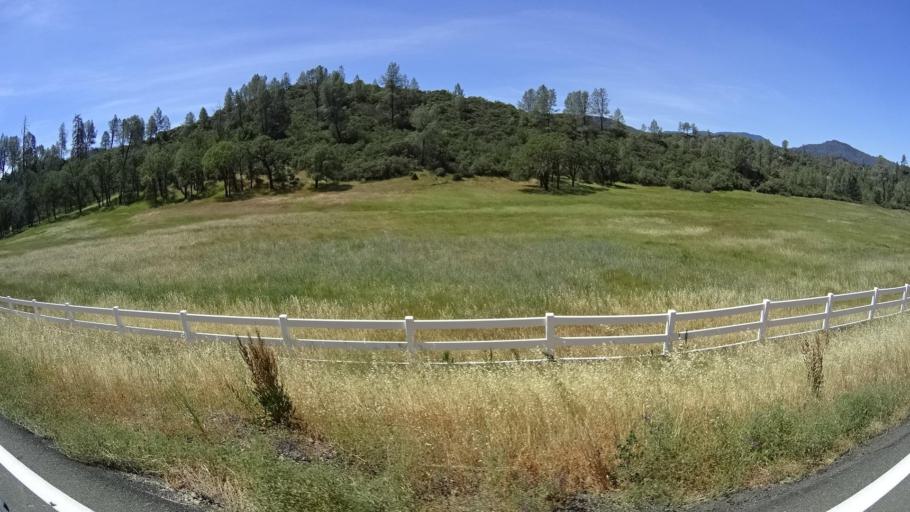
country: US
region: California
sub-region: Lake County
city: Hidden Valley Lake
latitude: 38.7209
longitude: -122.5033
